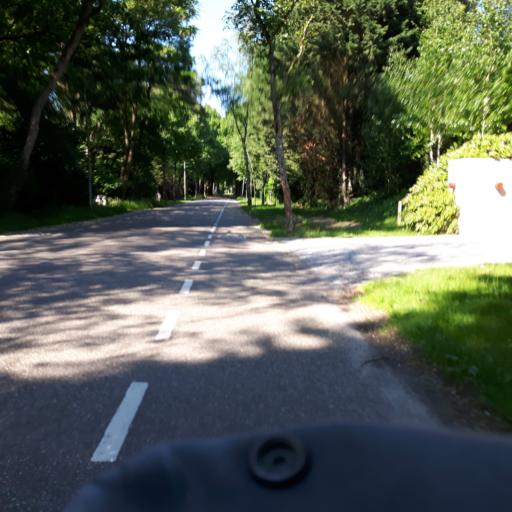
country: NL
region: Utrecht
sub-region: Gemeente Zeist
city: Zeist
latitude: 52.1344
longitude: 5.2402
